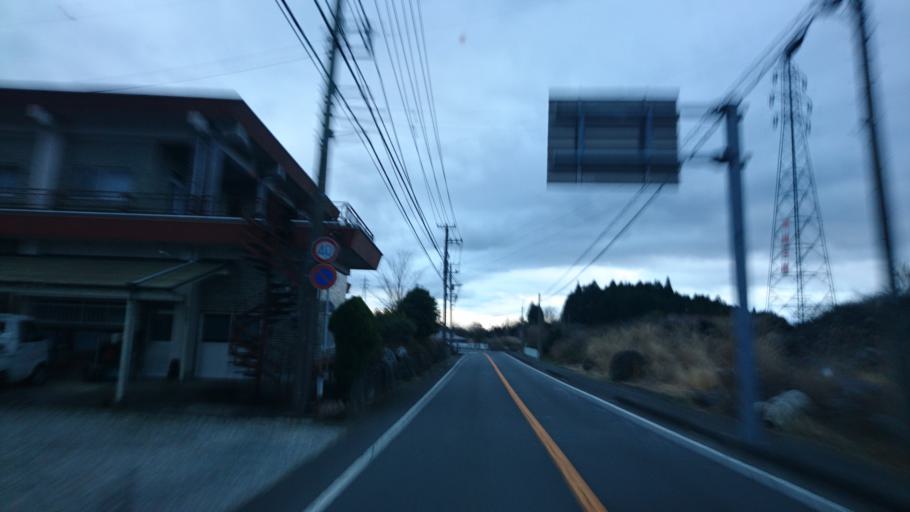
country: JP
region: Shizuoka
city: Fujinomiya
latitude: 35.3203
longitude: 138.5786
